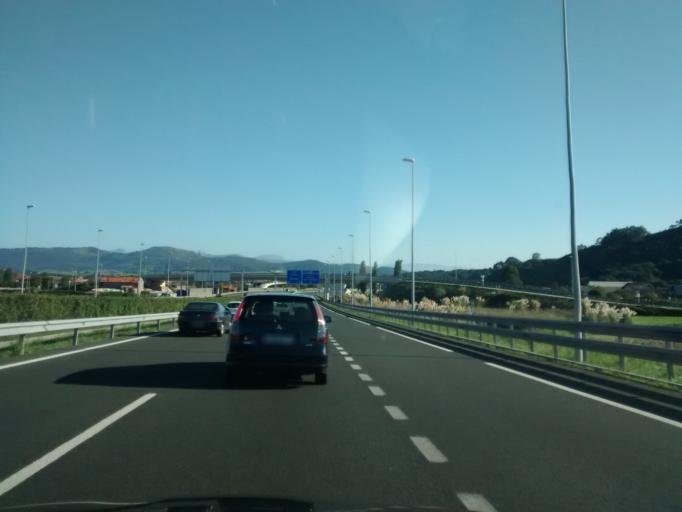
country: ES
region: Cantabria
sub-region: Provincia de Cantabria
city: Camargo
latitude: 43.4294
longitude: -3.8742
